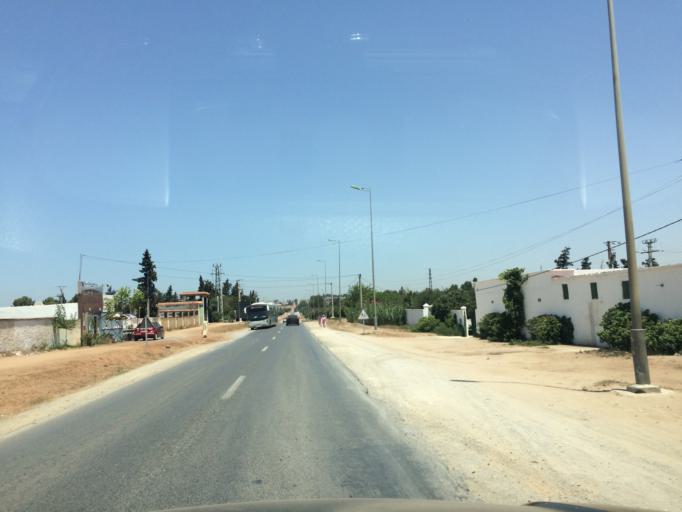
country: MA
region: Rabat-Sale-Zemmour-Zaer
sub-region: Skhirate-Temara
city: Temara
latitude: 33.8633
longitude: -6.8550
